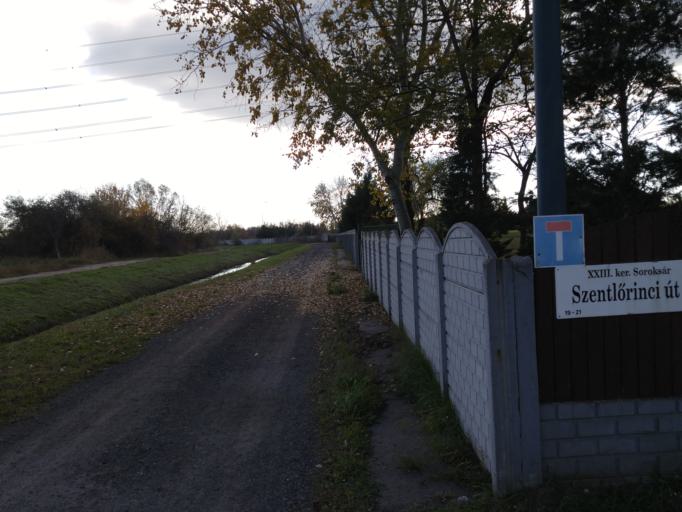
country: HU
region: Budapest
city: Budapest XXIII. keruelet
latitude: 47.4170
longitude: 19.1449
